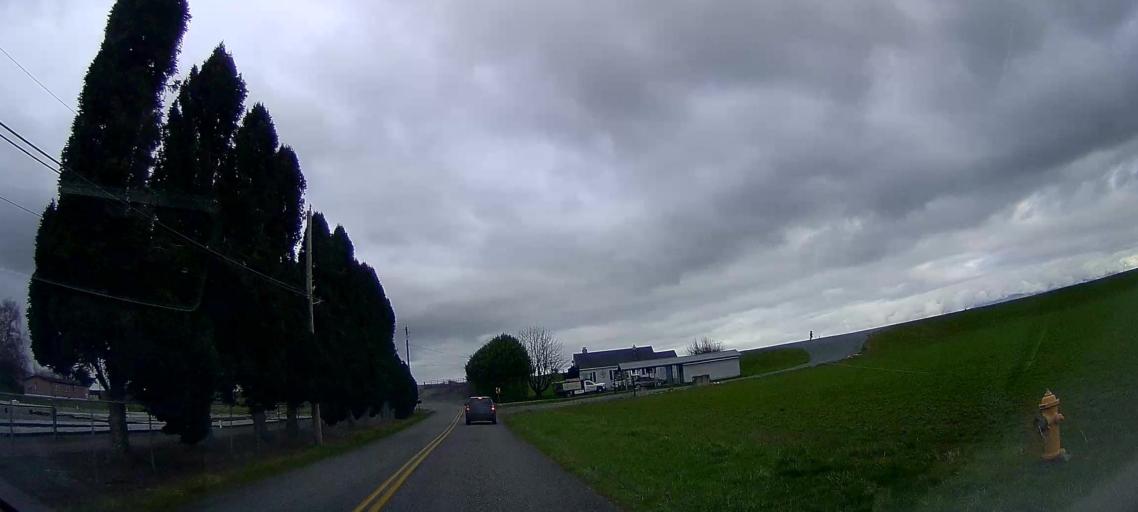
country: US
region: Washington
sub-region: Skagit County
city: Mount Vernon
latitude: 48.4455
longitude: -122.3574
